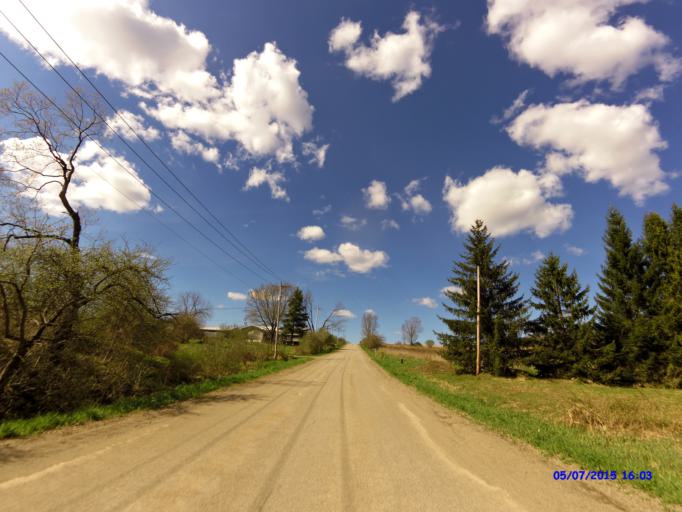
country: US
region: New York
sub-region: Cattaraugus County
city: Franklinville
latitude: 42.2934
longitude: -78.6146
